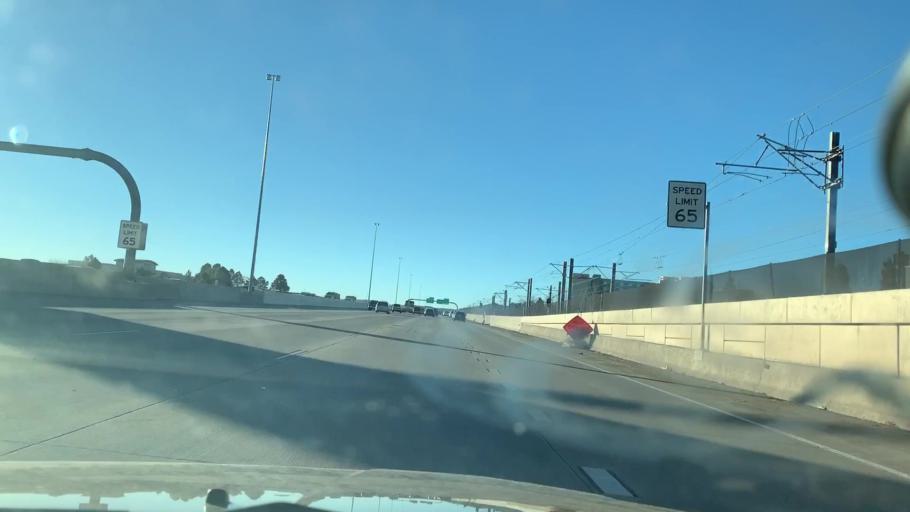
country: US
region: Colorado
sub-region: Douglas County
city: Meridian
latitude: 39.5451
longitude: -104.8697
